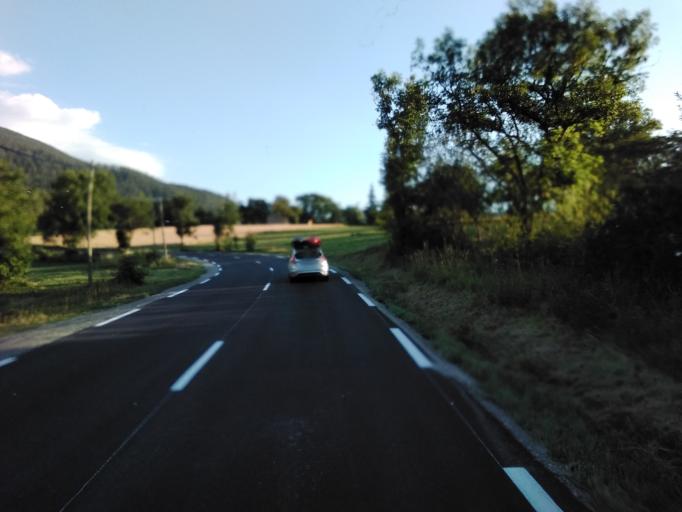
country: FR
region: Provence-Alpes-Cote d'Azur
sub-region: Departement des Alpes-de-Haute-Provence
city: Seyne-les-Alpes
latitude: 44.4456
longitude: 6.3644
